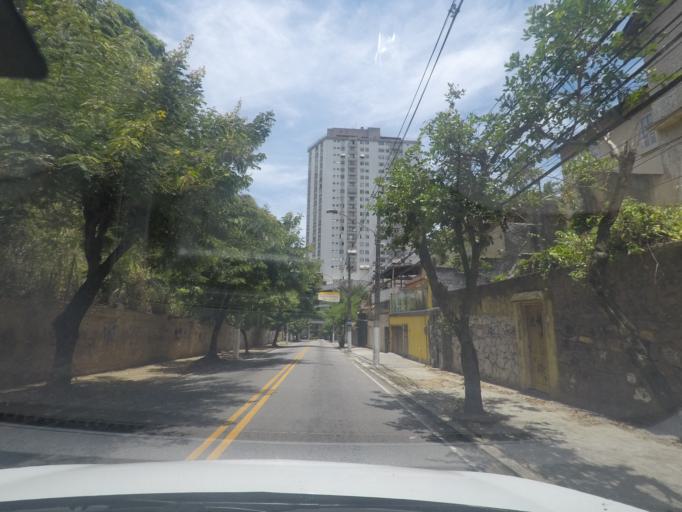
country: BR
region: Rio de Janeiro
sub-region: Niteroi
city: Niteroi
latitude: -22.9005
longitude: -43.1191
